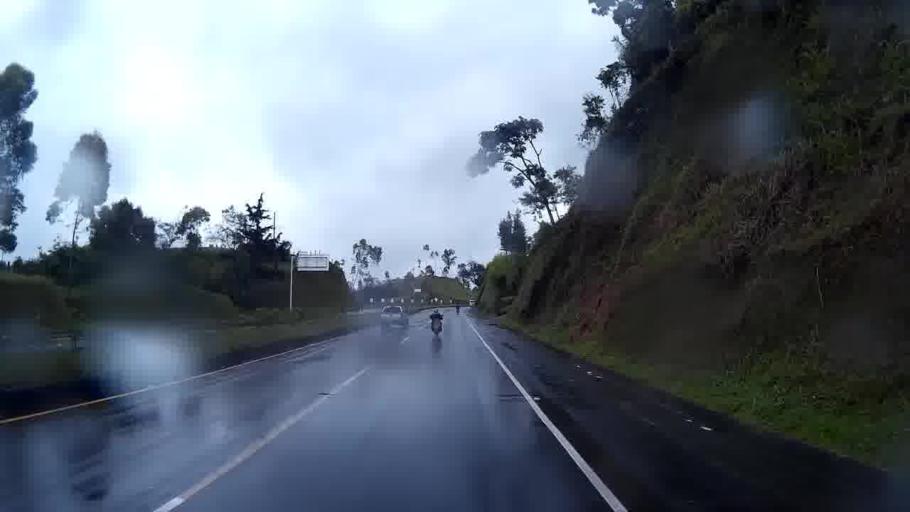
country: CO
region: Quindio
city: Filandia
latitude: 4.6828
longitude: -75.6046
